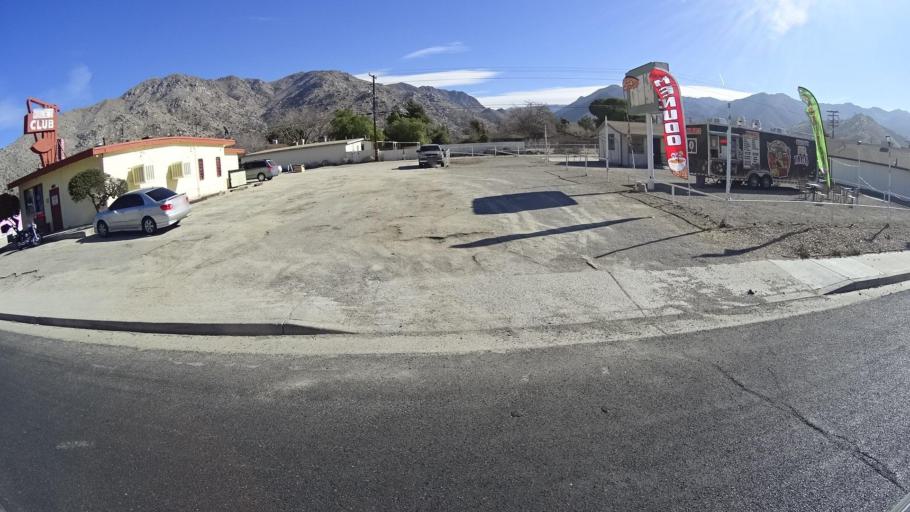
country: US
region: California
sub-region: Kern County
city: Lake Isabella
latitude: 35.6155
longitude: -118.4791
